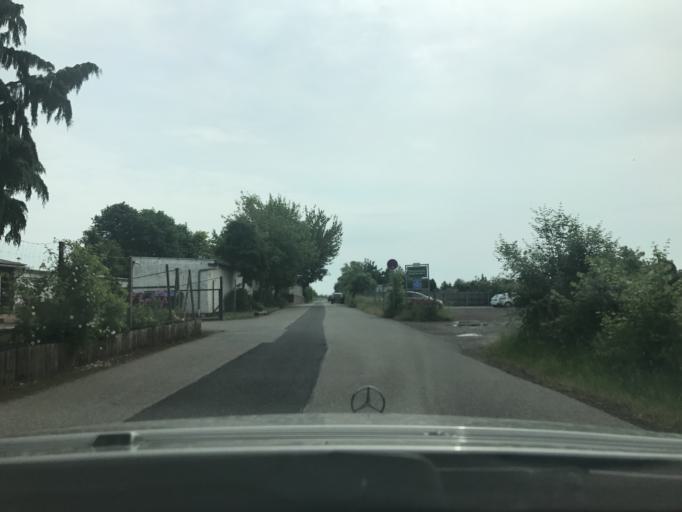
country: DE
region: Thuringia
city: Muehlhausen
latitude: 51.2312
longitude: 10.4830
